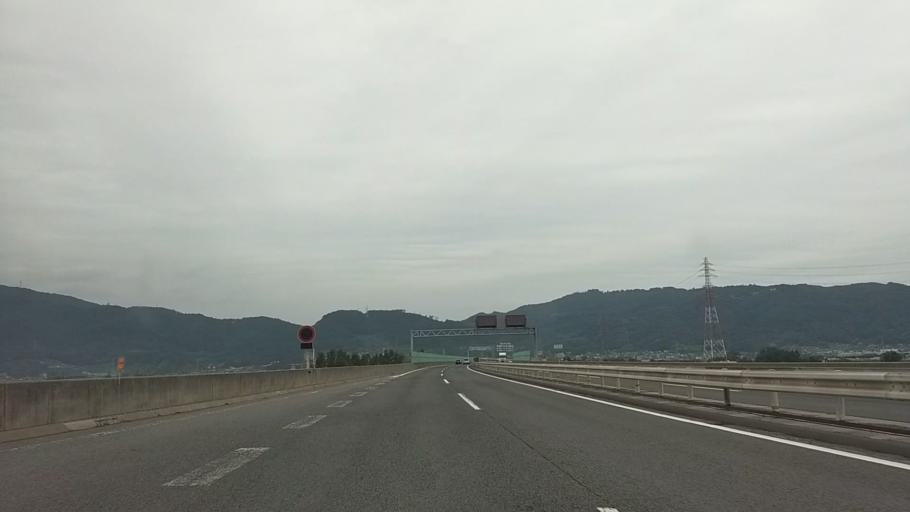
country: JP
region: Nagano
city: Nagano-shi
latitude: 36.5528
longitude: 138.1290
